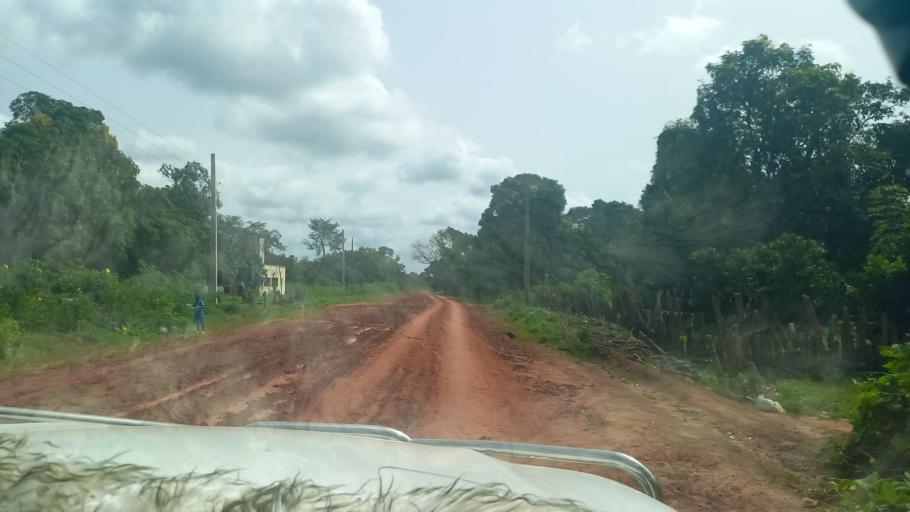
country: SN
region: Ziguinchor
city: Bignona
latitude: 12.7580
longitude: -16.2640
